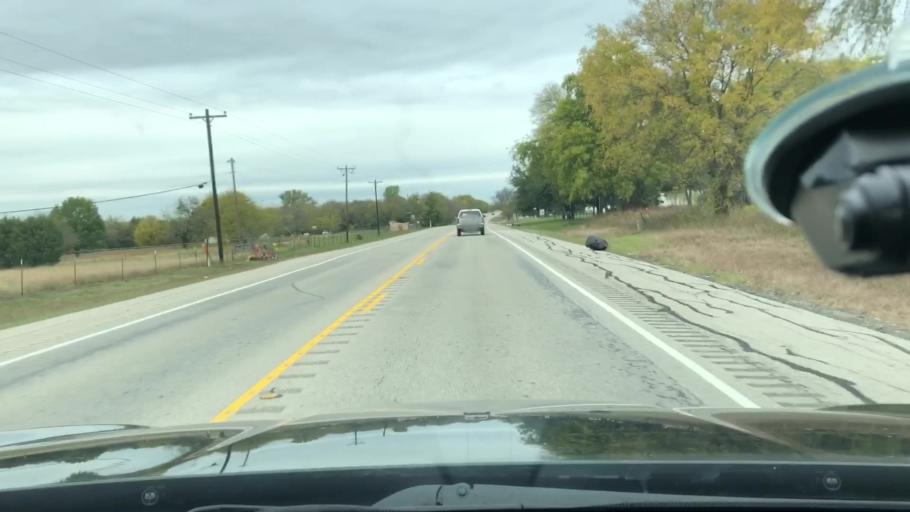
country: US
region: Texas
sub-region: Hunt County
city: Greenville
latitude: 33.0499
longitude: -96.1096
